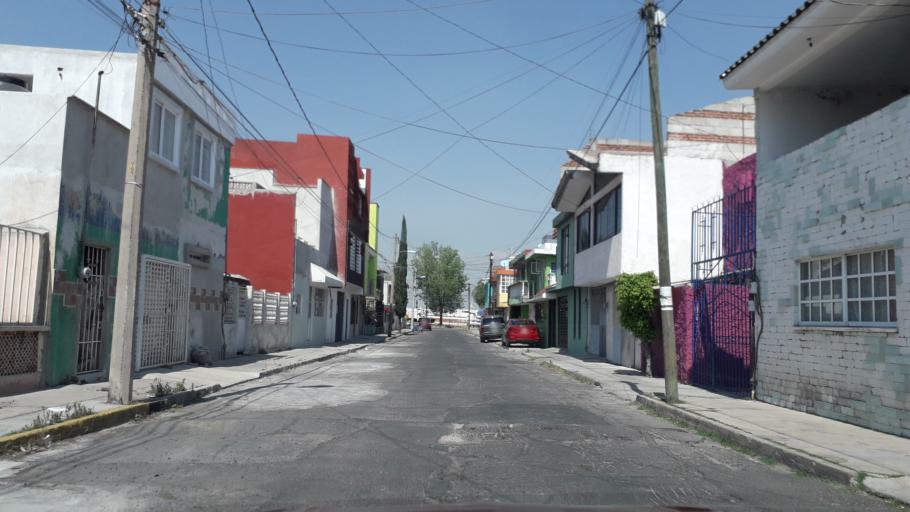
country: MX
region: Puebla
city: Puebla
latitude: 19.0787
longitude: -98.2157
